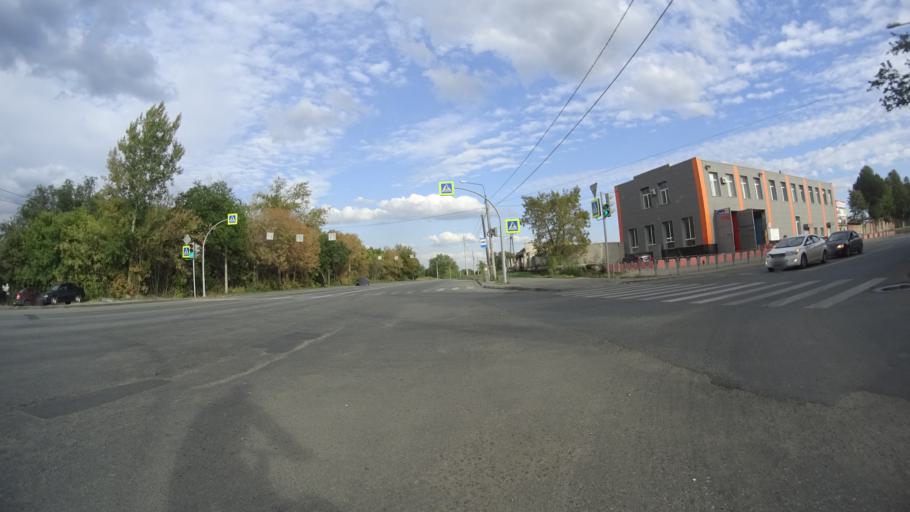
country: RU
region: Chelyabinsk
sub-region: Gorod Chelyabinsk
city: Chelyabinsk
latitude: 55.1971
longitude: 61.3711
